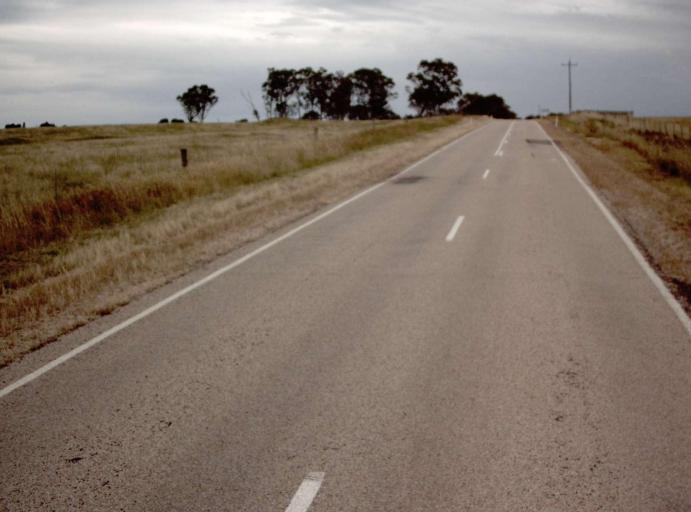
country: AU
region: Victoria
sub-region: East Gippsland
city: Bairnsdale
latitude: -37.8712
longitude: 147.5610
